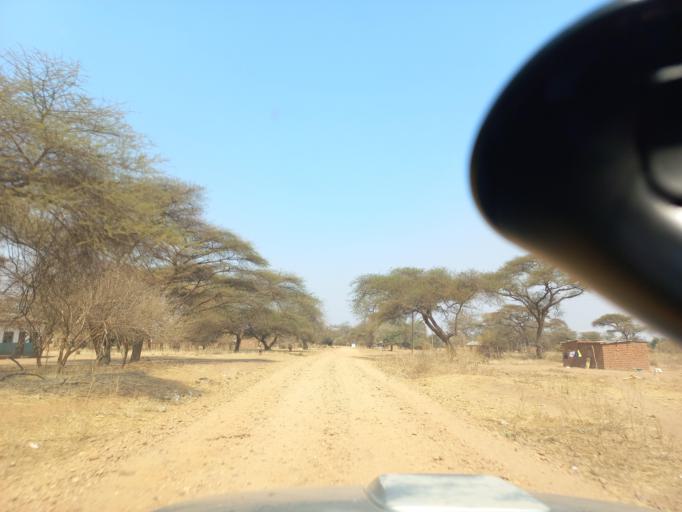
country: ZW
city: Chirundu
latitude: -15.9414
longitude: 28.8269
